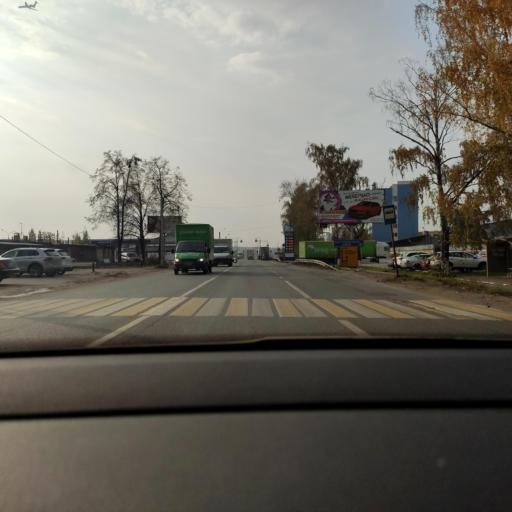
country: RU
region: Moskovskaya
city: Lesnyye Polyany
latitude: 55.9842
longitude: 37.8656
